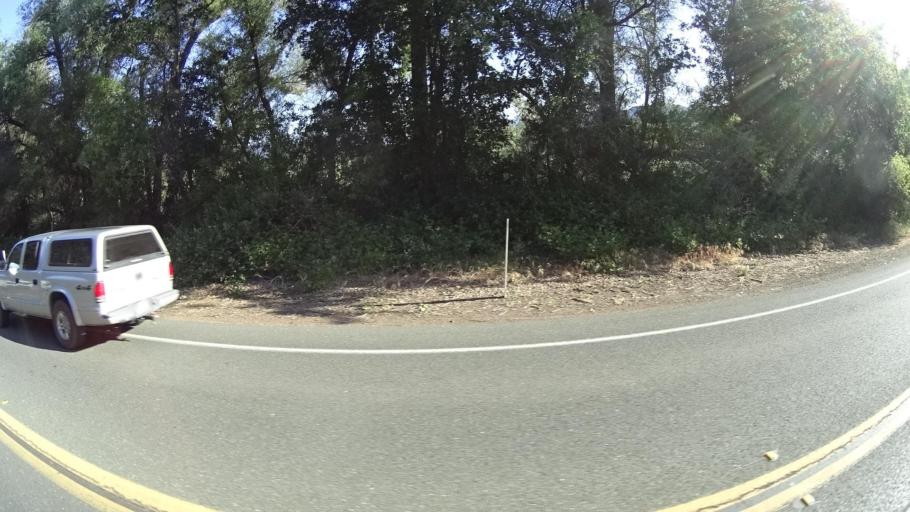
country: US
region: California
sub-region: Lake County
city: North Lakeport
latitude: 39.1180
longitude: -122.8882
